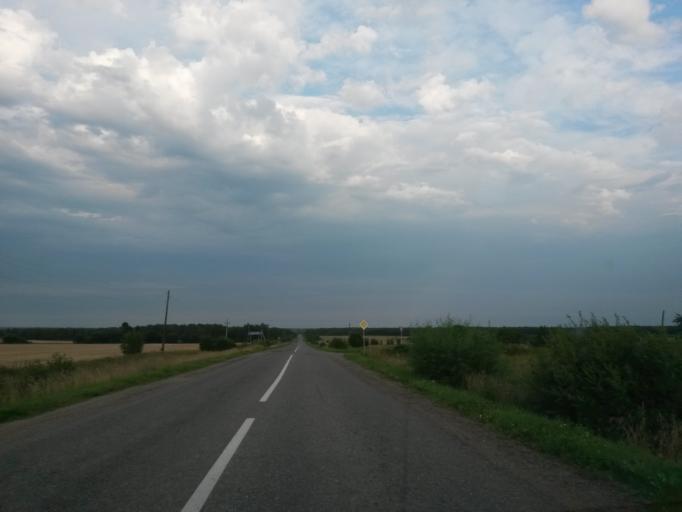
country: RU
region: Jaroslavl
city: Gavrilov-Yam
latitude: 57.3104
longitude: 39.9507
